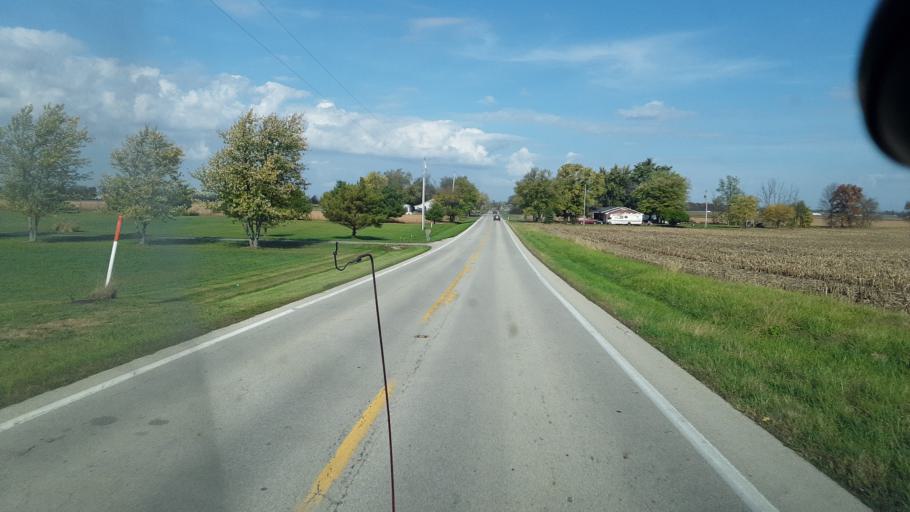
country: US
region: Ohio
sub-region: Clinton County
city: Sabina
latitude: 39.5437
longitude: -83.7104
